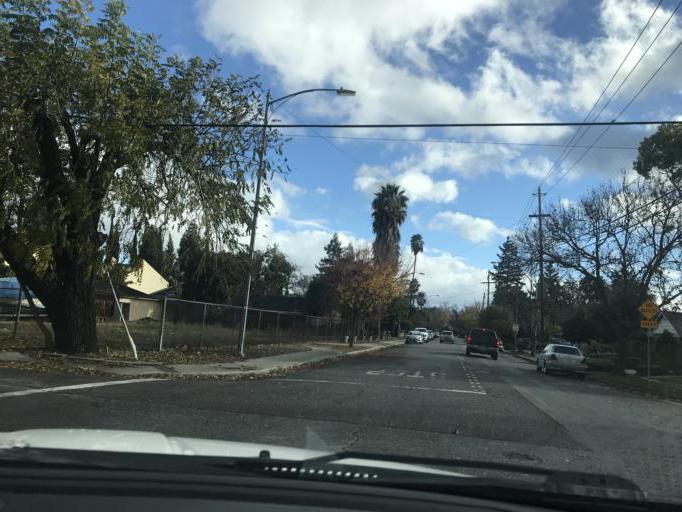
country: US
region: California
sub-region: Santa Clara County
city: Buena Vista
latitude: 37.3110
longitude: -121.9111
